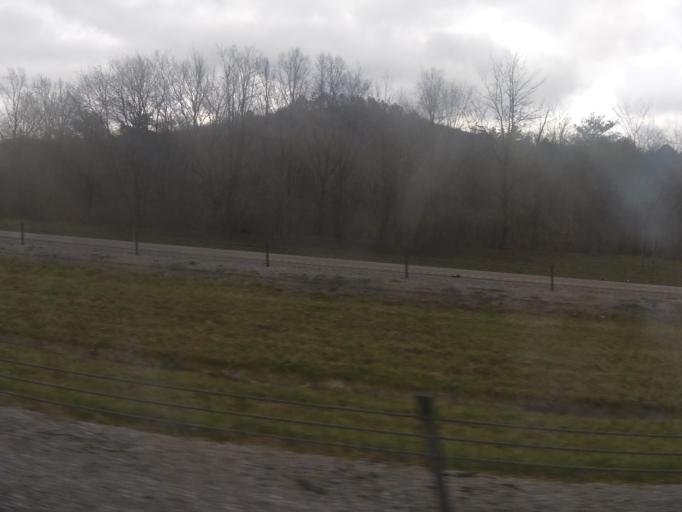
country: US
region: Georgia
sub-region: Walker County
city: Lookout Mountain
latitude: 34.9874
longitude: -85.4698
